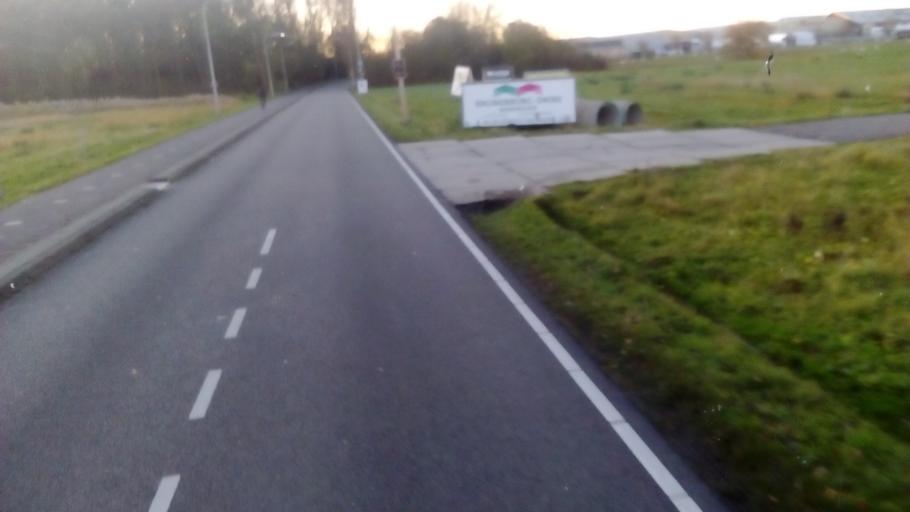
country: NL
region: South Holland
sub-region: Gemeente Westland
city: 's-Gravenzande
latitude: 52.0052
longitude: 4.1798
